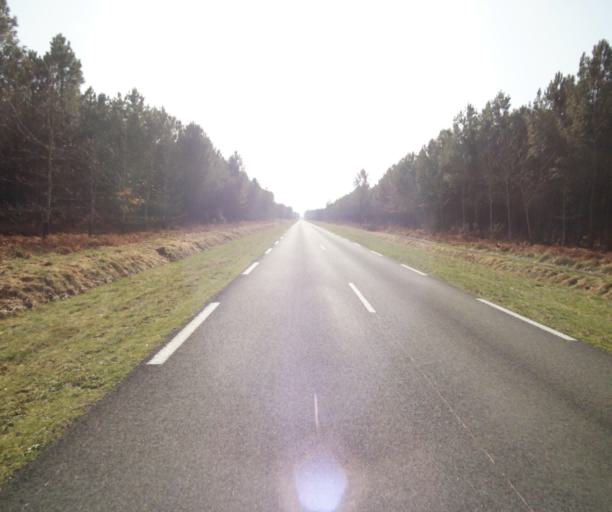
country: FR
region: Aquitaine
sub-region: Departement de la Gironde
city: Grignols
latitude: 44.1885
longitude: -0.1452
